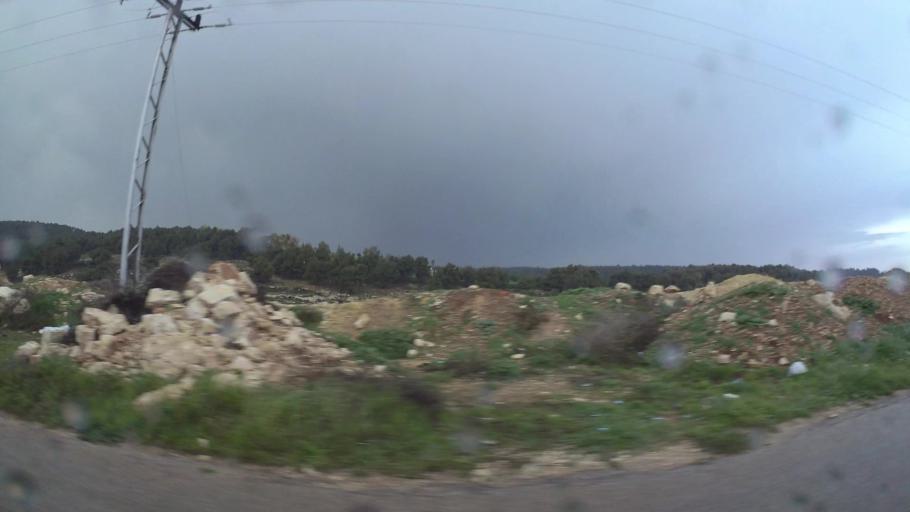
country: JO
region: Amman
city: Umm as Summaq
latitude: 31.8618
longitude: 35.8732
